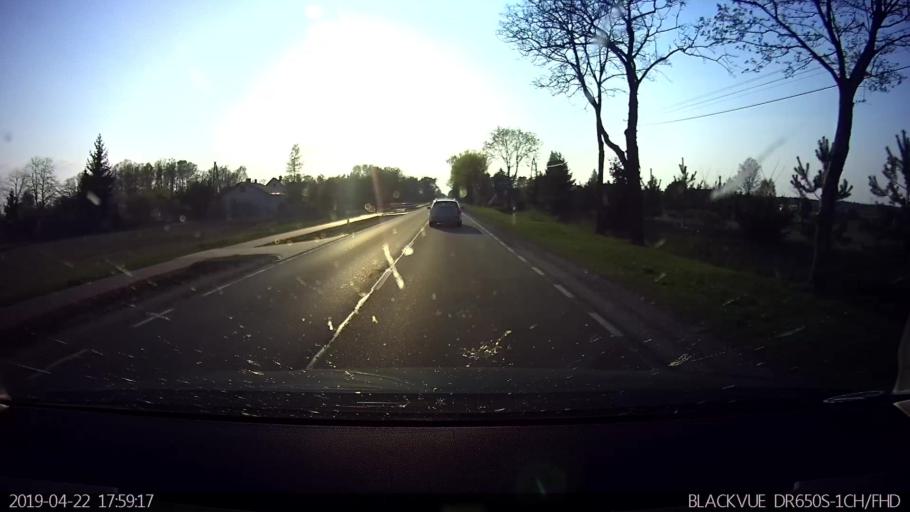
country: PL
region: Masovian Voivodeship
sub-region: Powiat wegrowski
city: Korytnica
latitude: 52.4733
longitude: 21.8657
